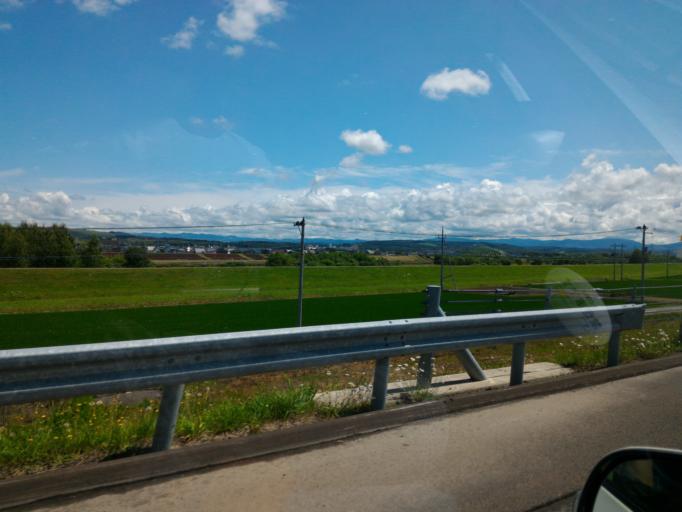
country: JP
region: Hokkaido
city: Nayoro
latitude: 44.3512
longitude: 142.4357
